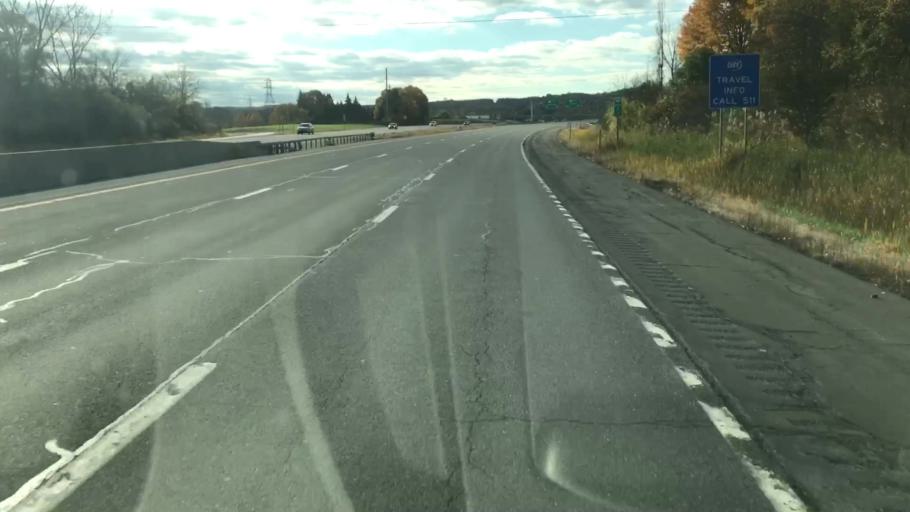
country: US
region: New York
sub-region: Onondaga County
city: Fairmount
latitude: 43.0649
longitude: -76.2361
